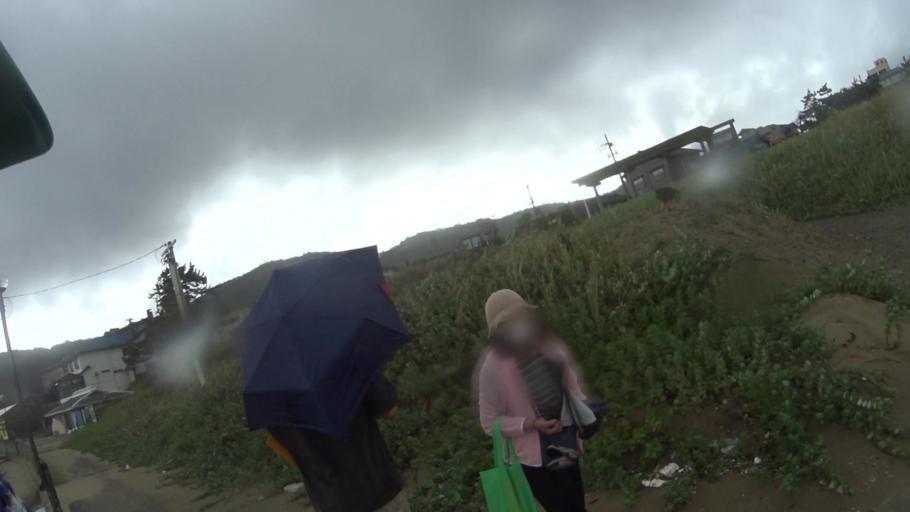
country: JP
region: Hyogo
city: Toyooka
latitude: 35.6639
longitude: 134.9652
